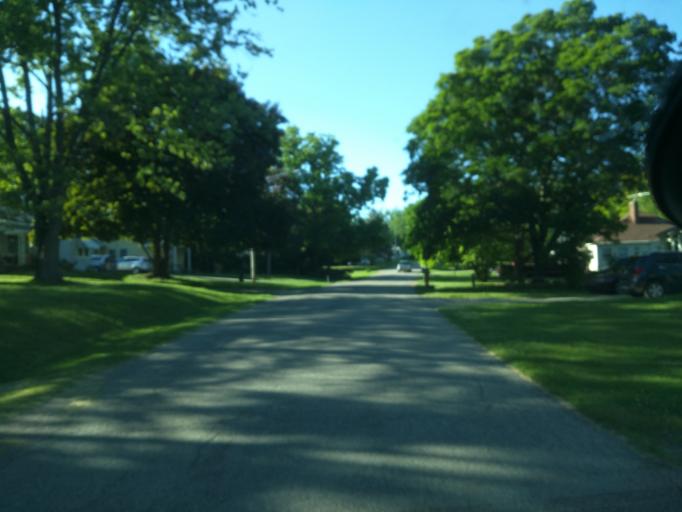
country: US
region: Michigan
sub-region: Ingham County
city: Edgemont Park
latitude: 42.7426
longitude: -84.5948
